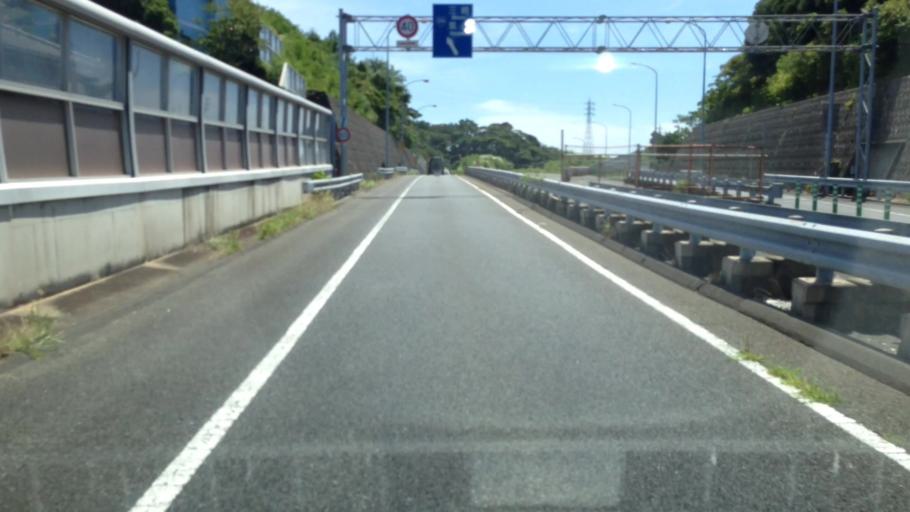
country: JP
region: Kanagawa
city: Yokosuka
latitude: 35.2155
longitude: 139.6374
